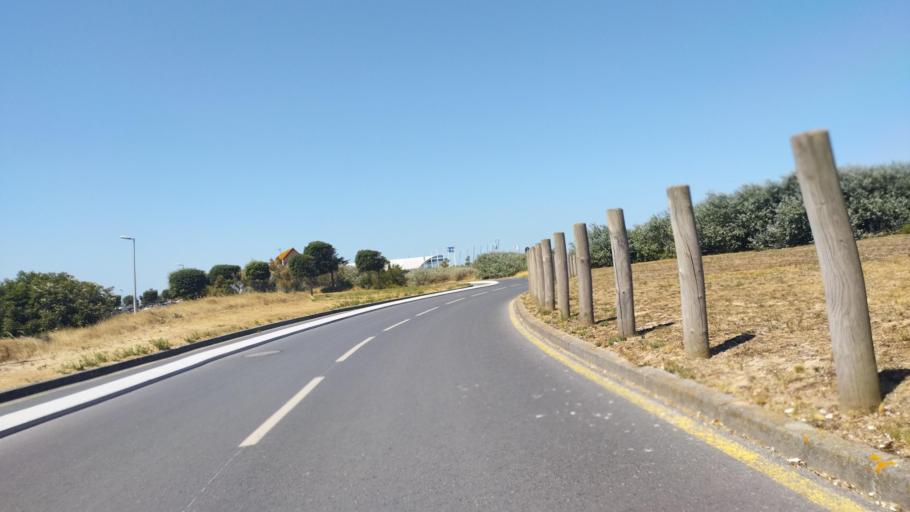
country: FR
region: Lower Normandy
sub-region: Departement du Calvados
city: Courseulles-sur-Mer
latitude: 49.3364
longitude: -0.4624
